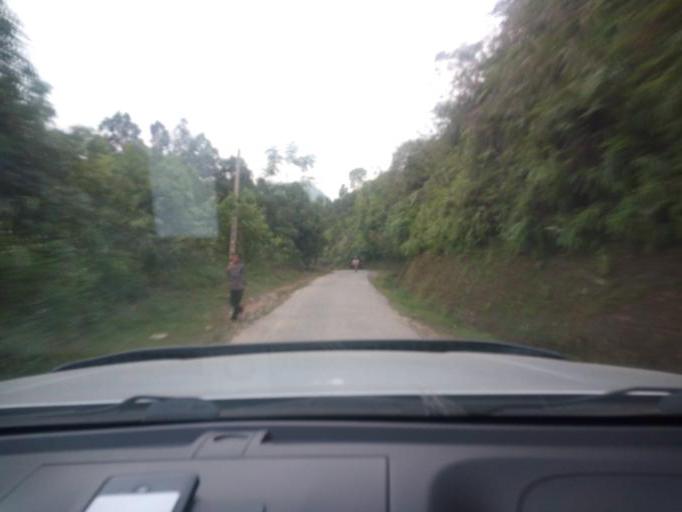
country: VN
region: Yen Bai
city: Co Phuc
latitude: 21.8337
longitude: 104.6220
